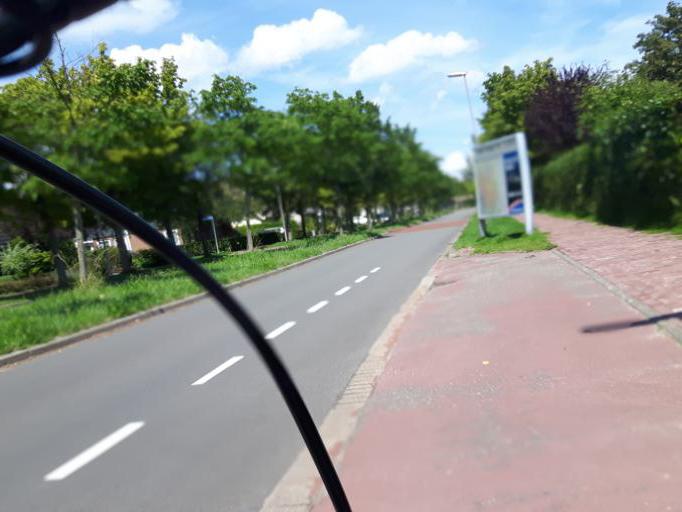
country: NL
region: Zeeland
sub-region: Gemeente Goes
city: Goes
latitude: 51.5106
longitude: 3.9019
